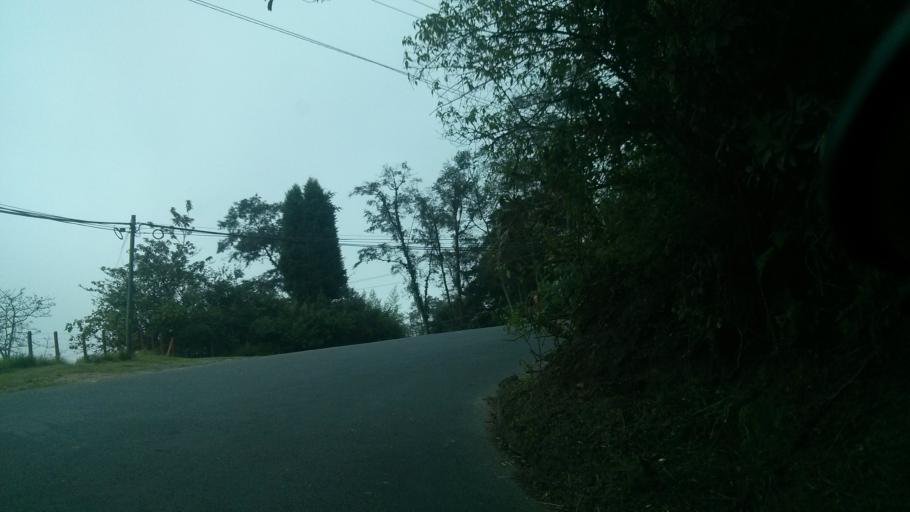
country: CR
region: San Jose
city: Ipis
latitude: 9.9925
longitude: -83.9608
